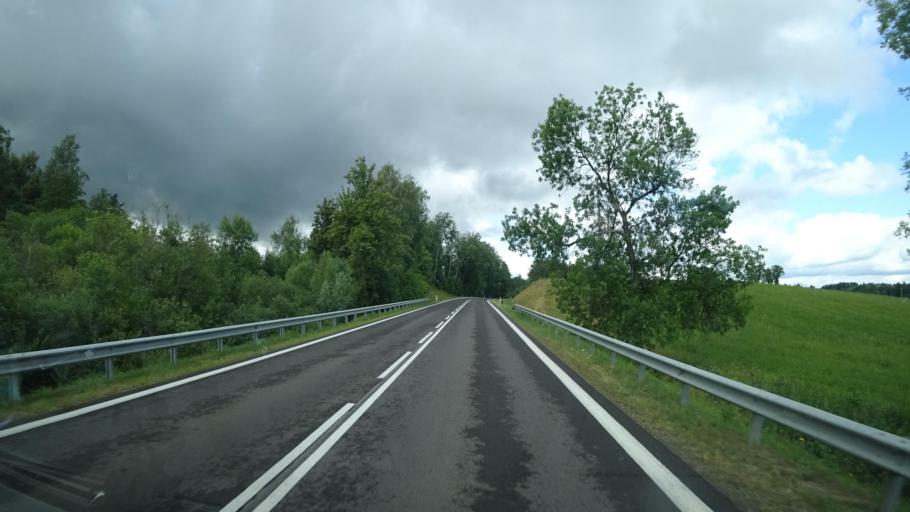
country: PL
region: Warmian-Masurian Voivodeship
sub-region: Powiat goldapski
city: Goldap
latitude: 54.2594
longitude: 22.3665
